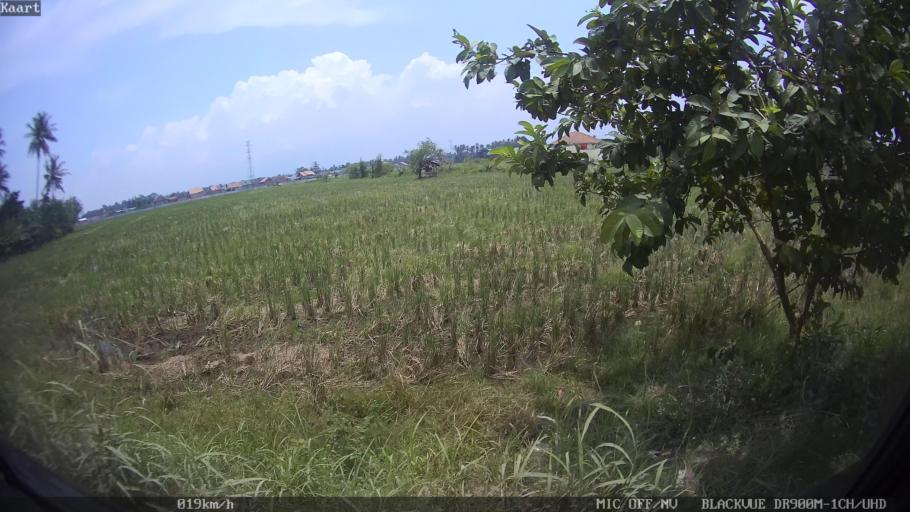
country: ID
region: Lampung
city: Kedaton
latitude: -5.3324
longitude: 105.2466
